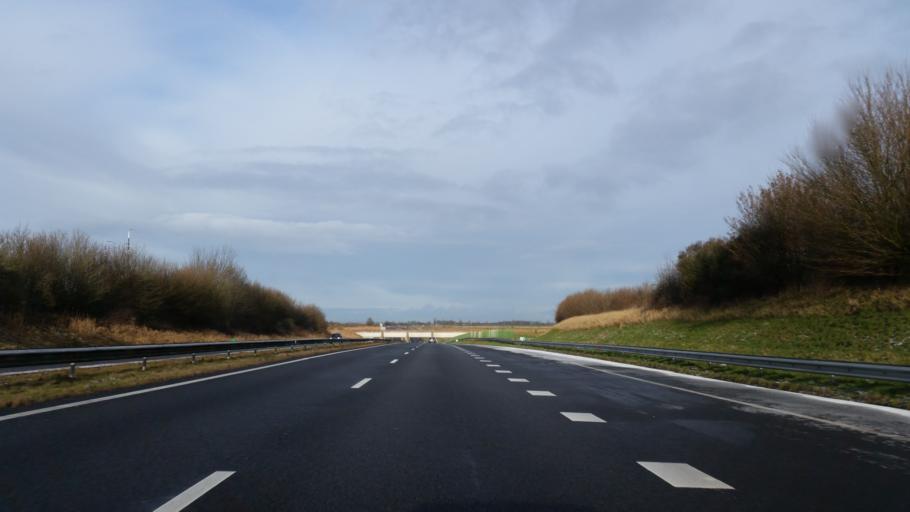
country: NL
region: Friesland
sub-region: Gemeente Boarnsterhim
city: Nes
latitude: 53.0528
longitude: 5.8435
